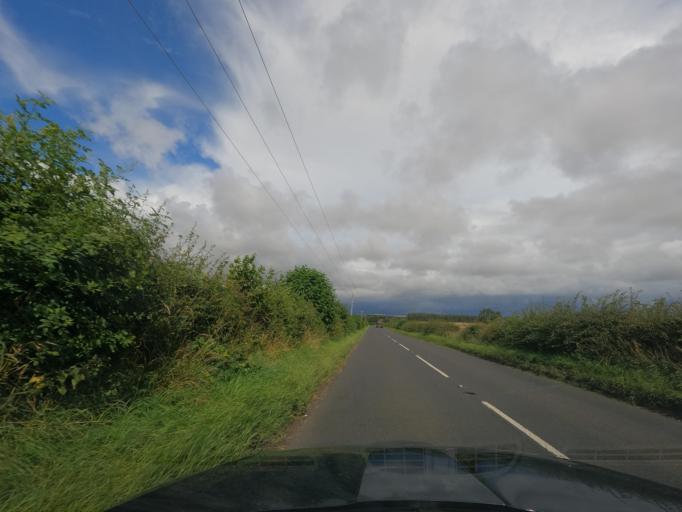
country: GB
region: England
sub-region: Northumberland
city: Ancroft
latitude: 55.6661
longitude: -1.9992
